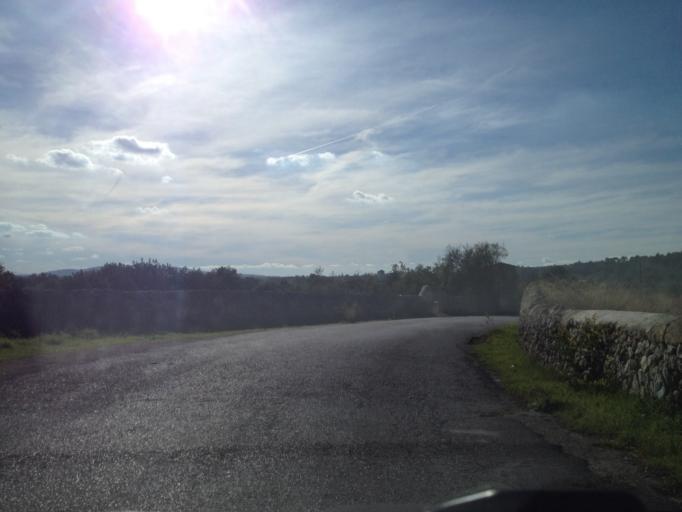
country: ES
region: Balearic Islands
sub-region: Illes Balears
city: Lloseta
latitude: 39.7159
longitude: 2.8591
